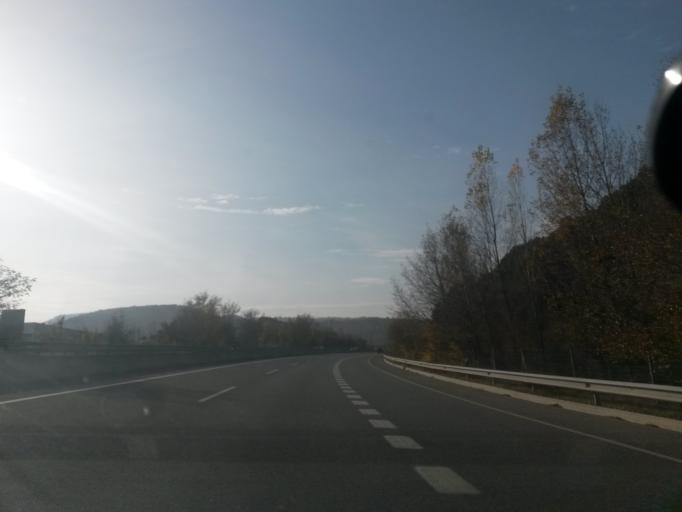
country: ES
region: Catalonia
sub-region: Provincia de Girona
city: Sant Joan les Fonts
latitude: 42.2045
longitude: 2.5377
